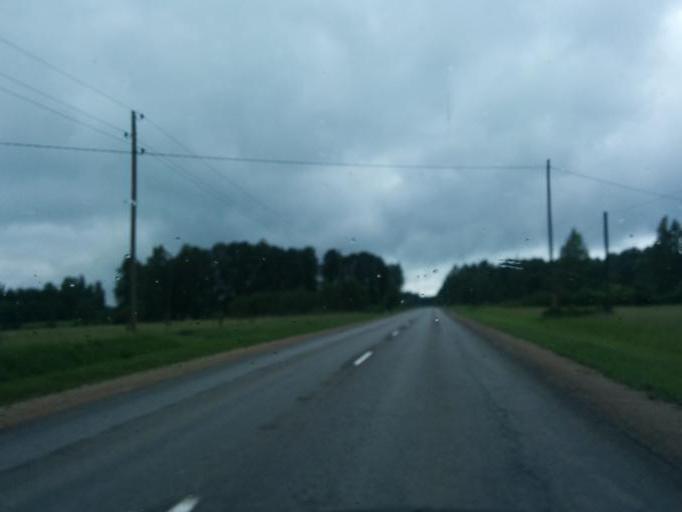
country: LV
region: Smiltene
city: Smiltene
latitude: 57.3963
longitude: 25.9636
